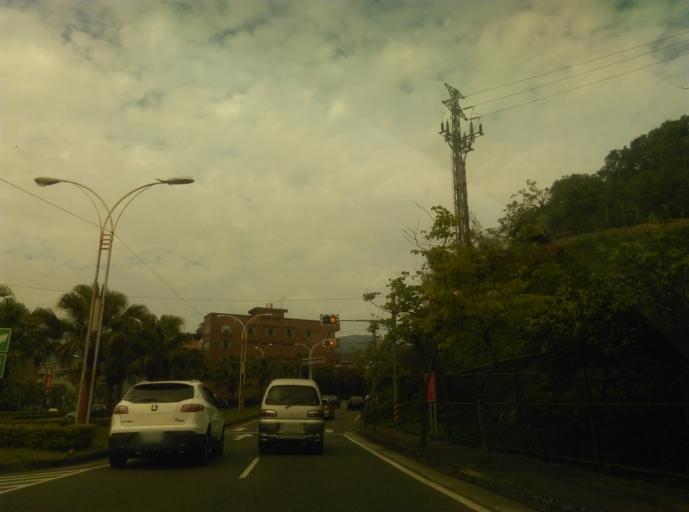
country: TW
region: Taiwan
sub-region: Keelung
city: Keelung
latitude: 25.1554
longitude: 121.6966
